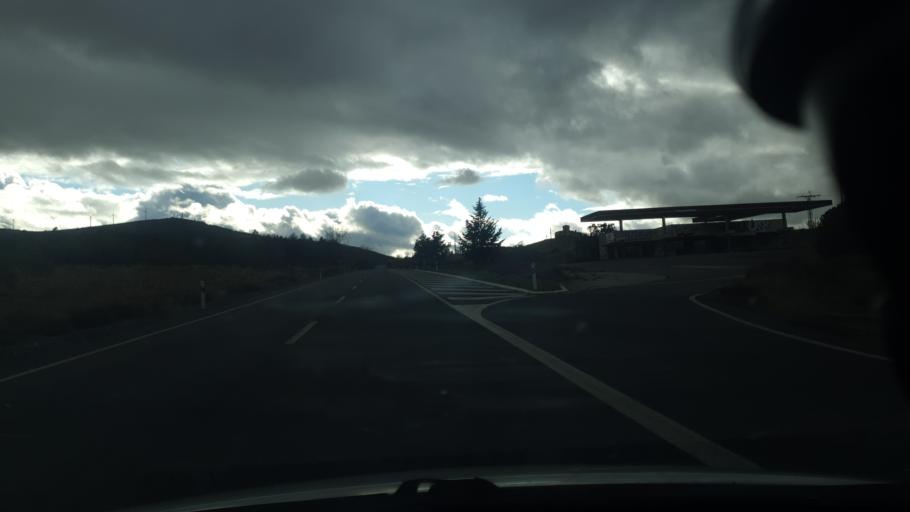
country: ES
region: Castille and Leon
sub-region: Provincia de Segovia
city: Villacastin
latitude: 40.7495
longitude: -4.4575
